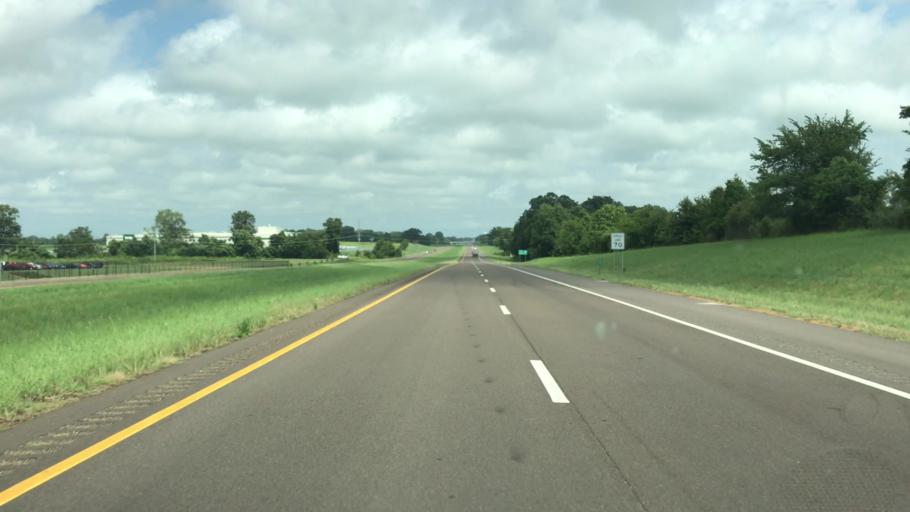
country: US
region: Tennessee
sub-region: Dyer County
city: Dyersburg
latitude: 36.0772
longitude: -89.3415
